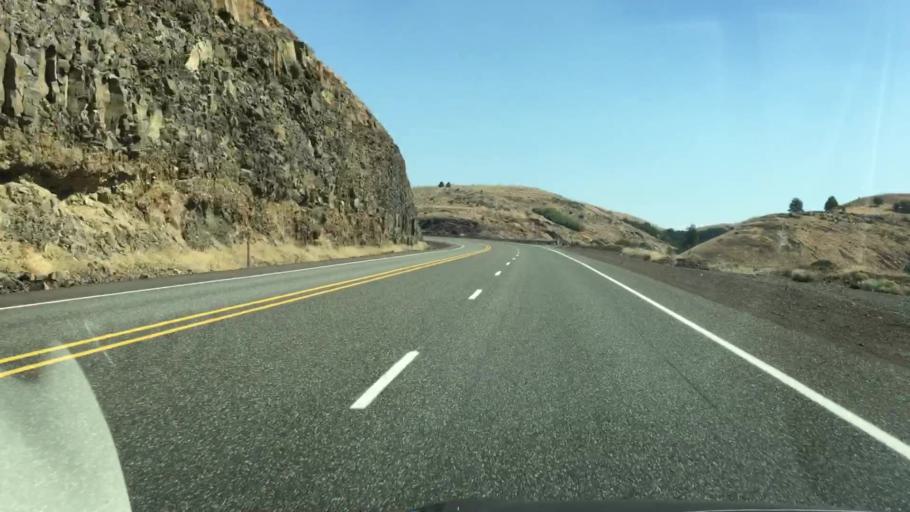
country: US
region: Oregon
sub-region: Wasco County
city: The Dalles
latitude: 45.3019
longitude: -121.1520
